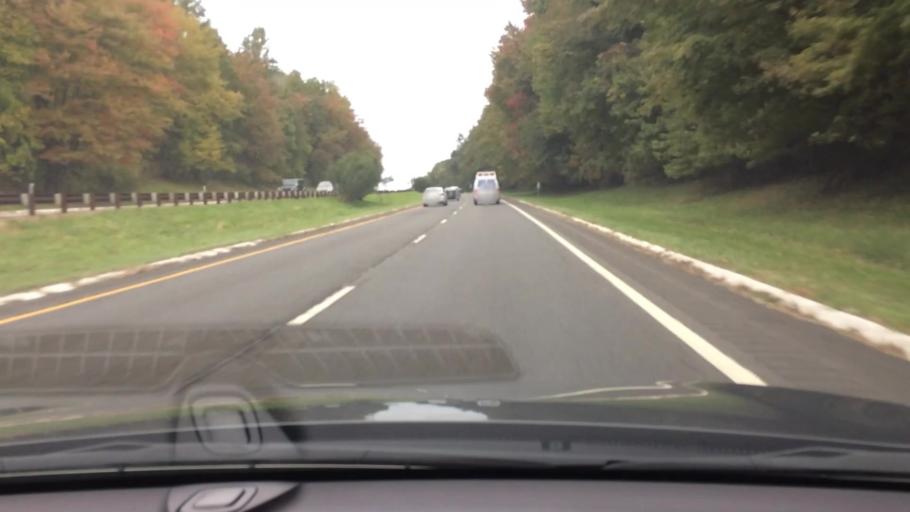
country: US
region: New York
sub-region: Rockland County
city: West Nyack
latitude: 41.0732
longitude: -73.9817
